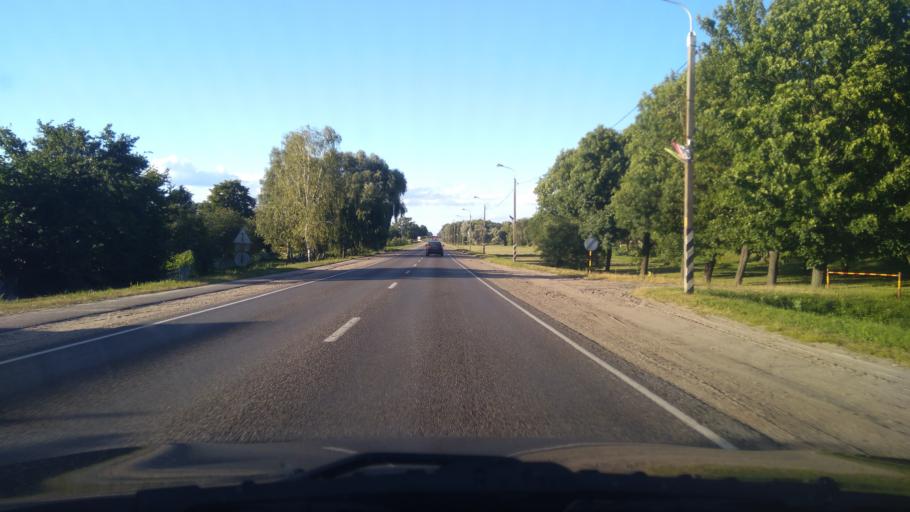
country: BY
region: Brest
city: Pruzhany
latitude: 52.5559
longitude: 24.4766
